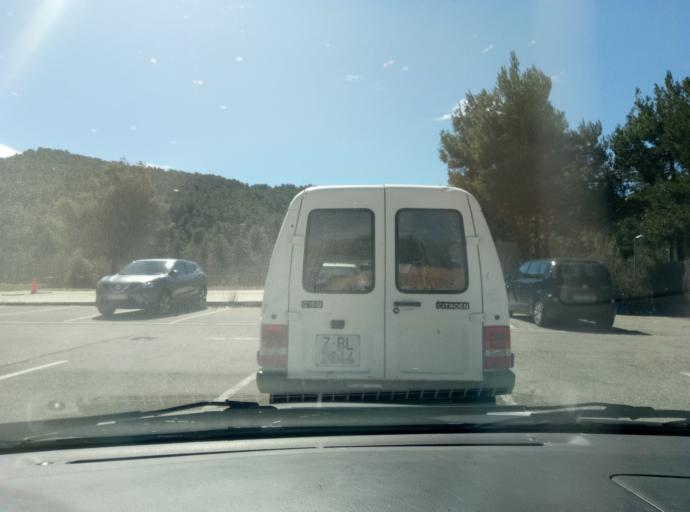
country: ES
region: Catalonia
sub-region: Provincia de Lleida
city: Nalec
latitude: 41.5084
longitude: 1.1363
